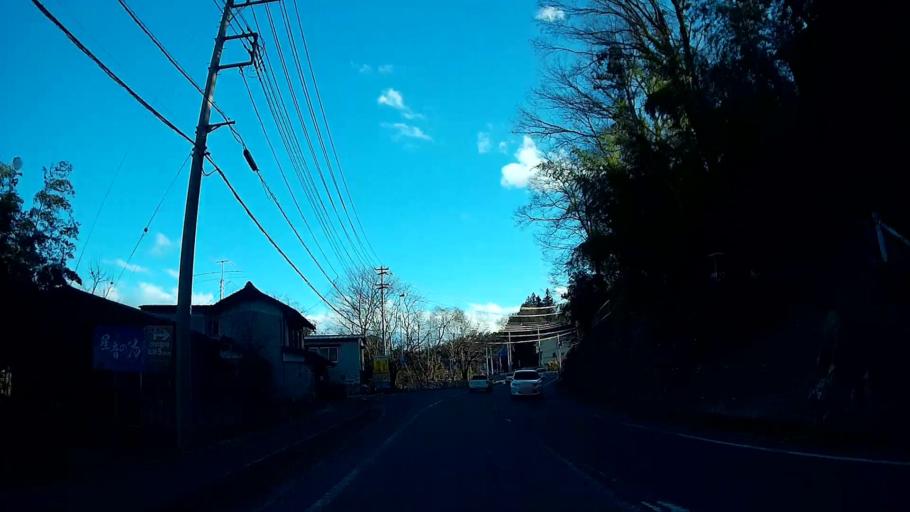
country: JP
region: Saitama
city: Chichibu
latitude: 36.0655
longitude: 139.0863
